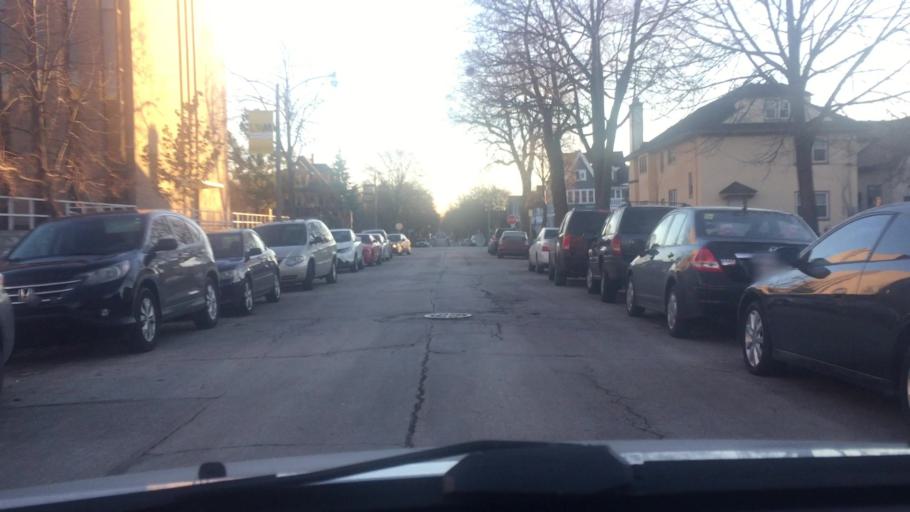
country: US
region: Wisconsin
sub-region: Milwaukee County
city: Shorewood
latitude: 43.0755
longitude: -87.8866
